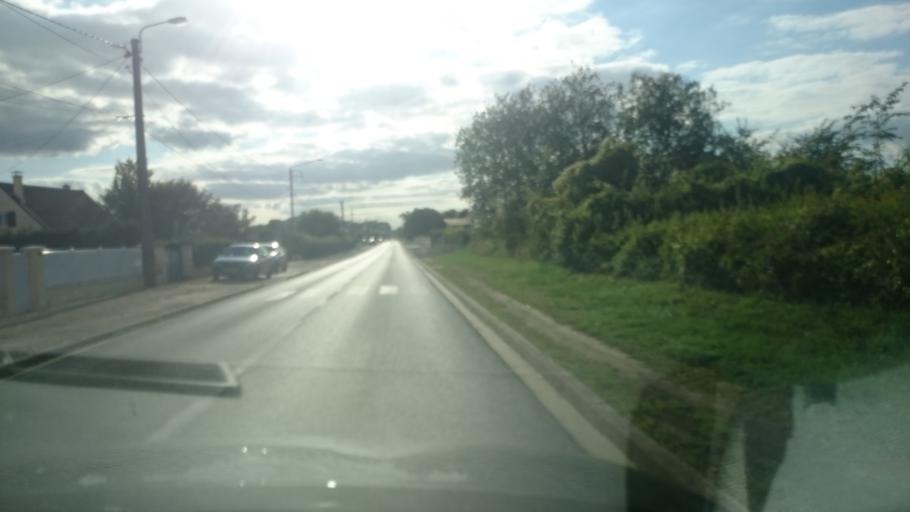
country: FR
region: Picardie
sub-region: Departement de l'Aisne
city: Tergnier
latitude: 49.6043
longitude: 3.3046
